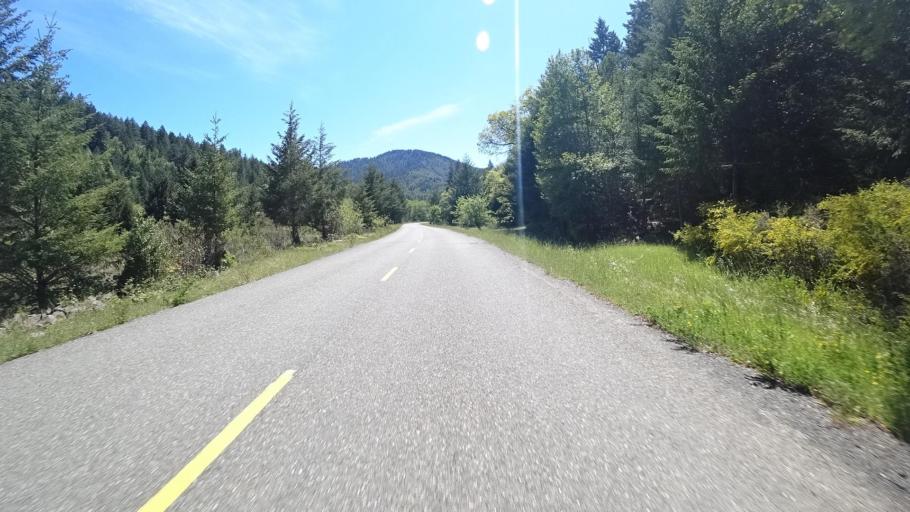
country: US
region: California
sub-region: Humboldt County
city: Rio Dell
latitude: 40.3426
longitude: -124.0268
